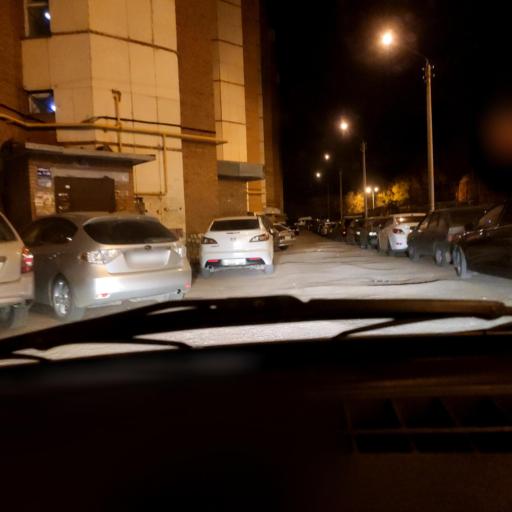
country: RU
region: Bashkortostan
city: Ufa
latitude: 54.8198
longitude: 56.1199
